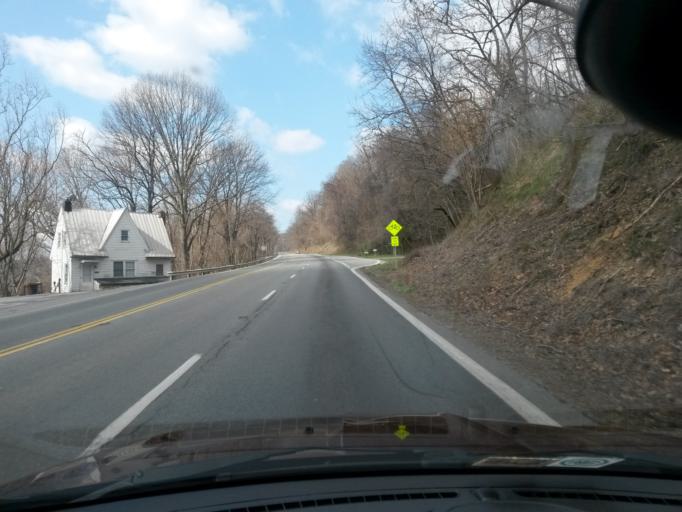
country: US
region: Virginia
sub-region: City of Waynesboro
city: Waynesboro
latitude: 38.0366
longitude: -78.8401
